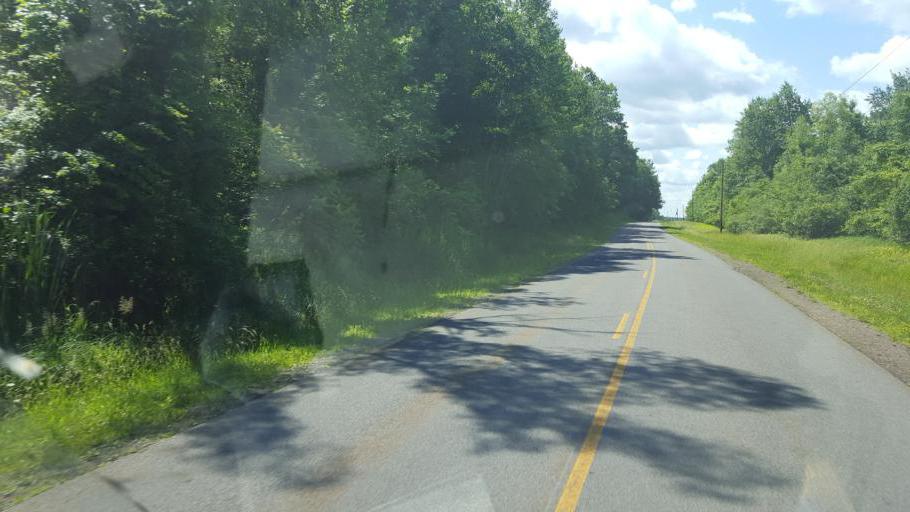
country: US
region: New York
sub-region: Wayne County
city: Wolcott
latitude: 43.2808
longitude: -76.9070
